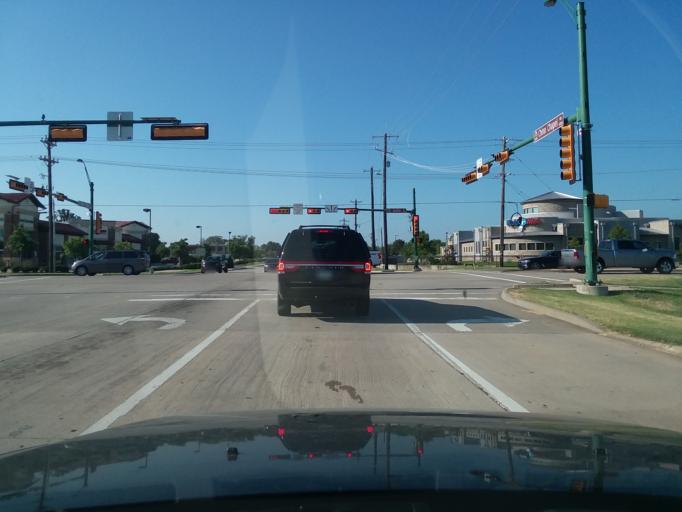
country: US
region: Texas
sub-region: Denton County
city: Double Oak
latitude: 33.0724
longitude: -97.0880
